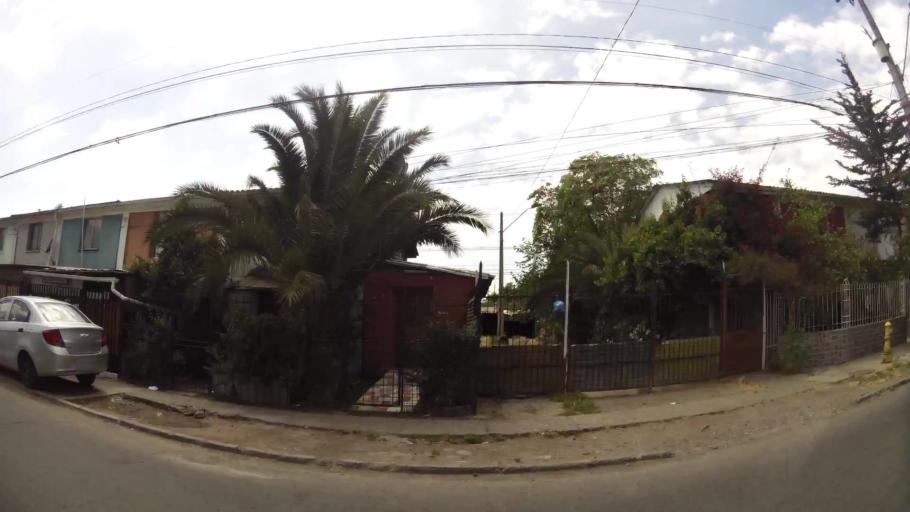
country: CL
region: Santiago Metropolitan
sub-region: Provincia de Santiago
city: Santiago
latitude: -33.5042
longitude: -70.6843
